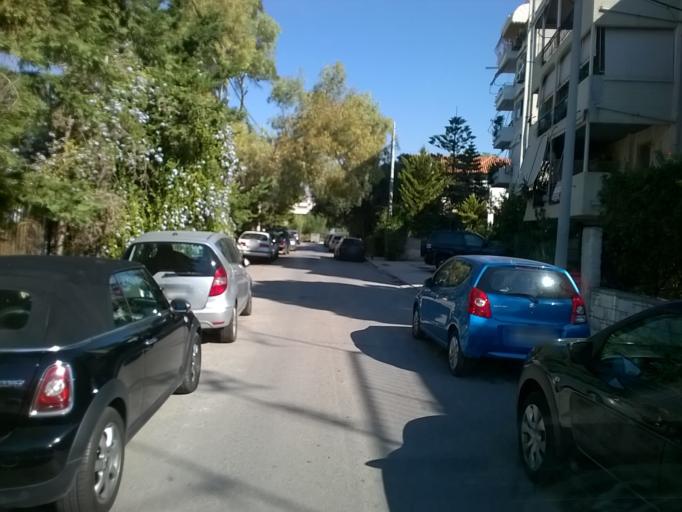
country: GR
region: Attica
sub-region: Nomarchia Anatolikis Attikis
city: Voula
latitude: 37.8303
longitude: 23.7721
